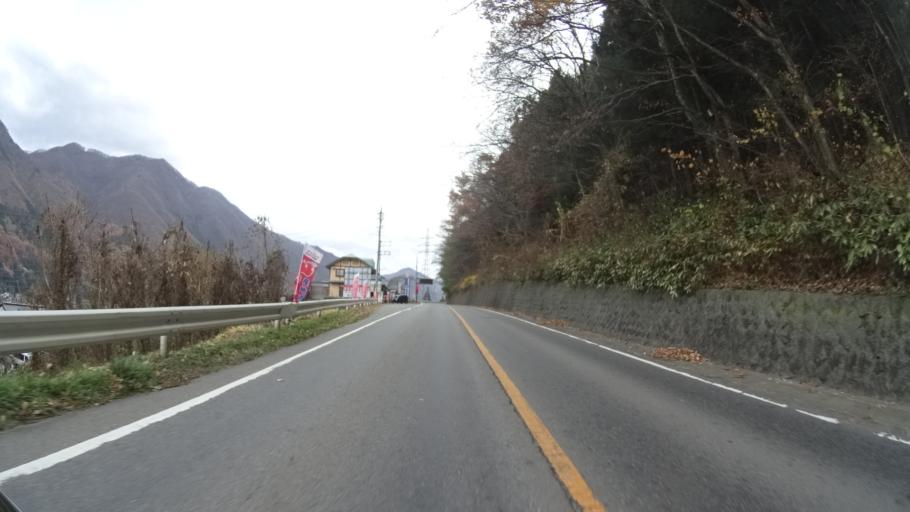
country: JP
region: Gunma
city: Numata
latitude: 36.6861
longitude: 139.2075
